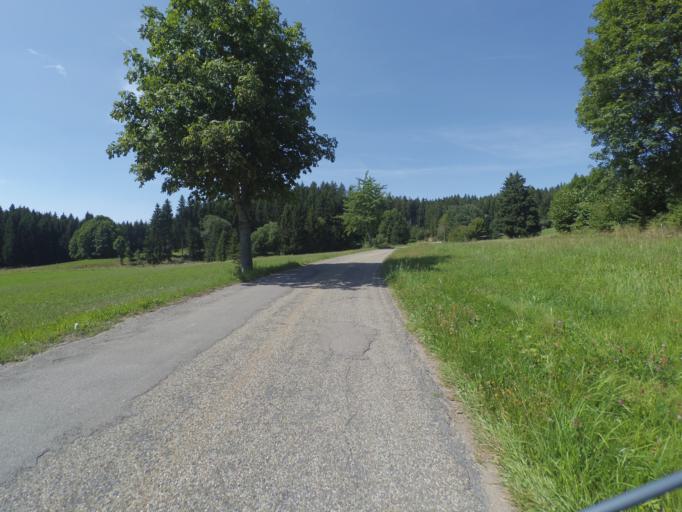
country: DE
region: Baden-Wuerttemberg
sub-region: Freiburg Region
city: Lenzkirch
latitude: 47.8813
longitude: 8.2142
